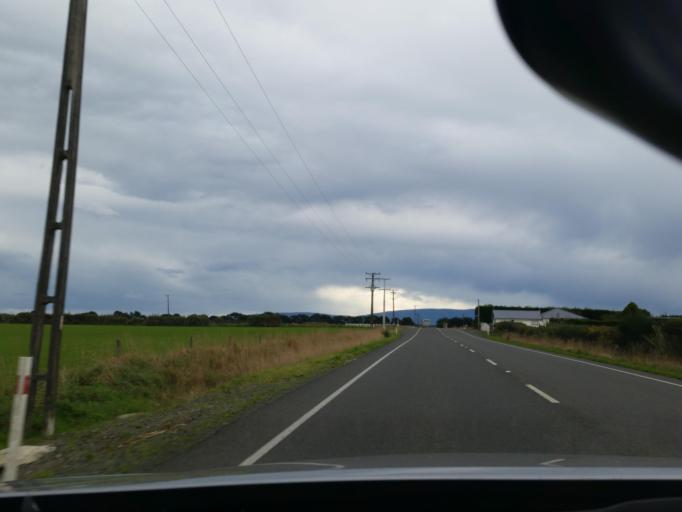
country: NZ
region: Southland
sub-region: Southland District
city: Riverton
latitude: -46.2982
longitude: 168.1563
